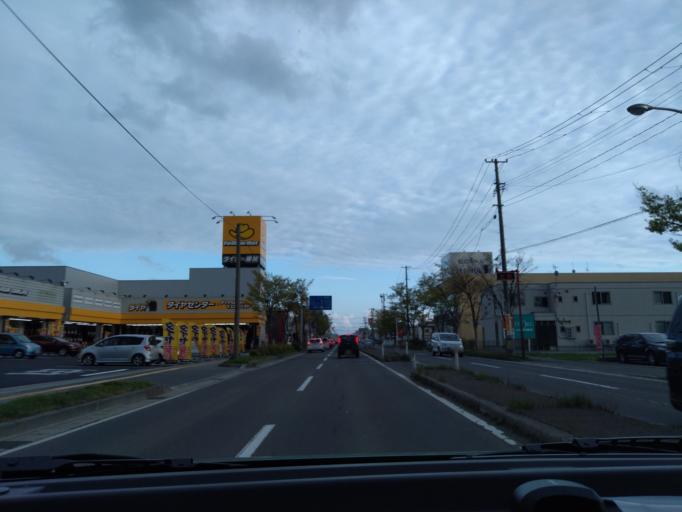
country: JP
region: Akita
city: Akita
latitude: 39.7276
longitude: 140.1476
